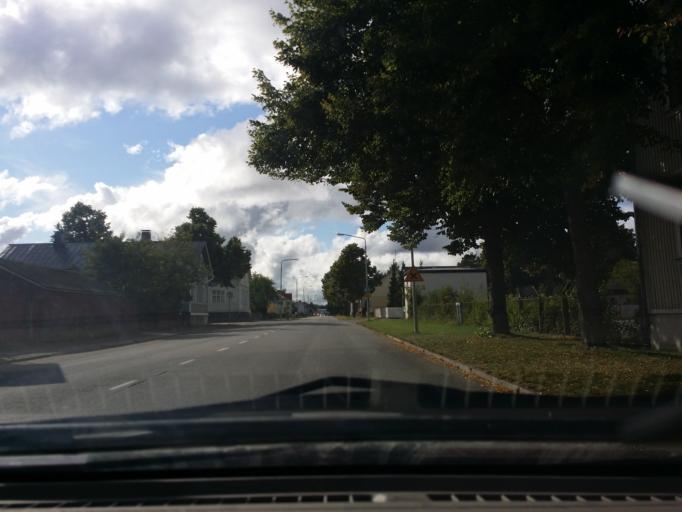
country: FI
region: Satakunta
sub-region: Pori
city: Pori
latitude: 61.4721
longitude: 21.8148
